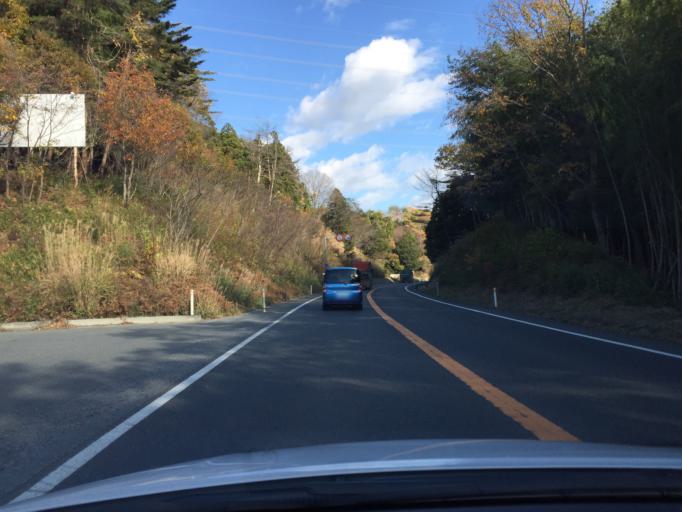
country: JP
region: Fukushima
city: Namie
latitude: 37.3148
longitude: 141.0008
